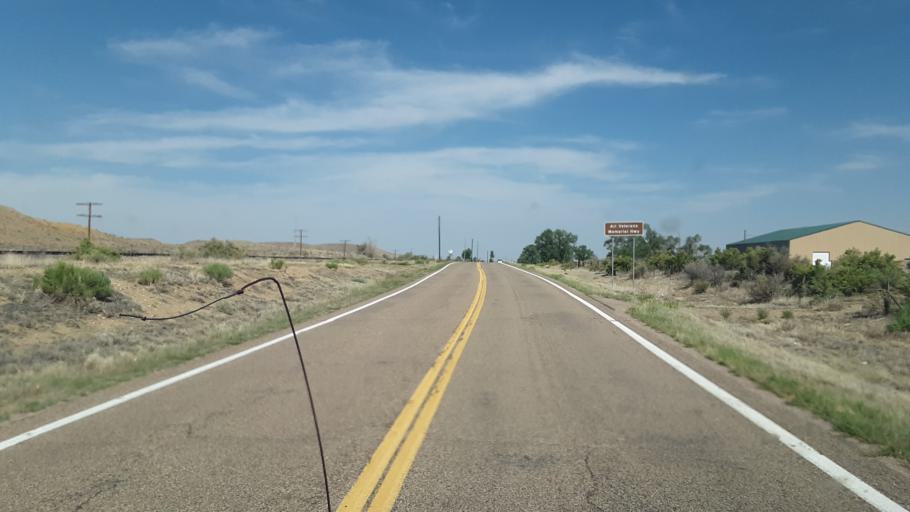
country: US
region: Colorado
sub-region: Otero County
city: Fowler
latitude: 38.1646
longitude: -104.0588
